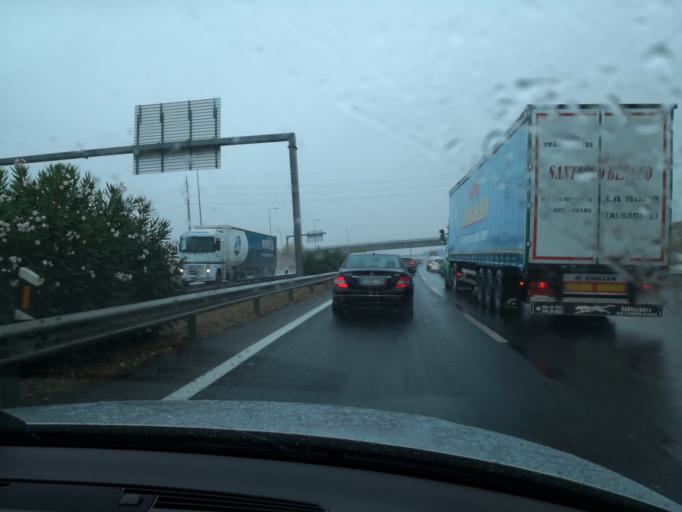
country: PT
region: Setubal
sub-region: Montijo
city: Montijo
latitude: 38.7022
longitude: -8.9407
